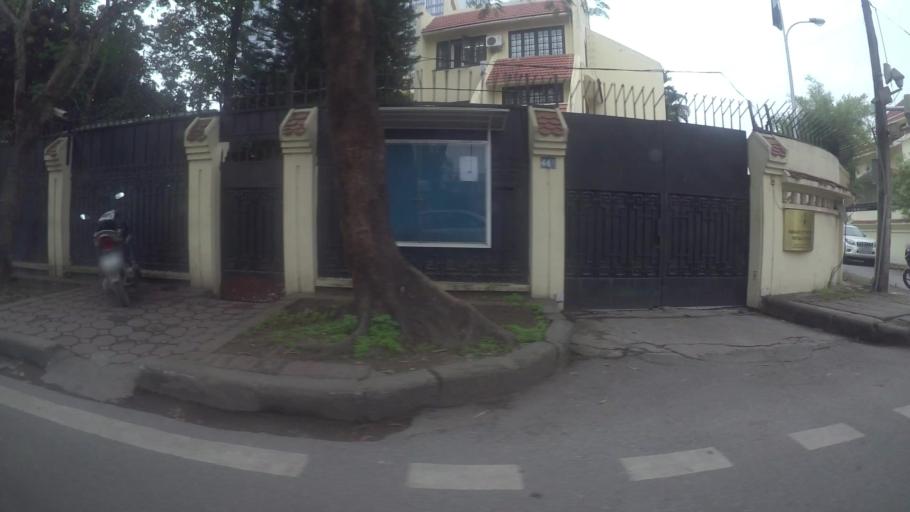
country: VN
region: Ha Noi
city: Cau Giay
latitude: 21.0322
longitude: 105.8171
